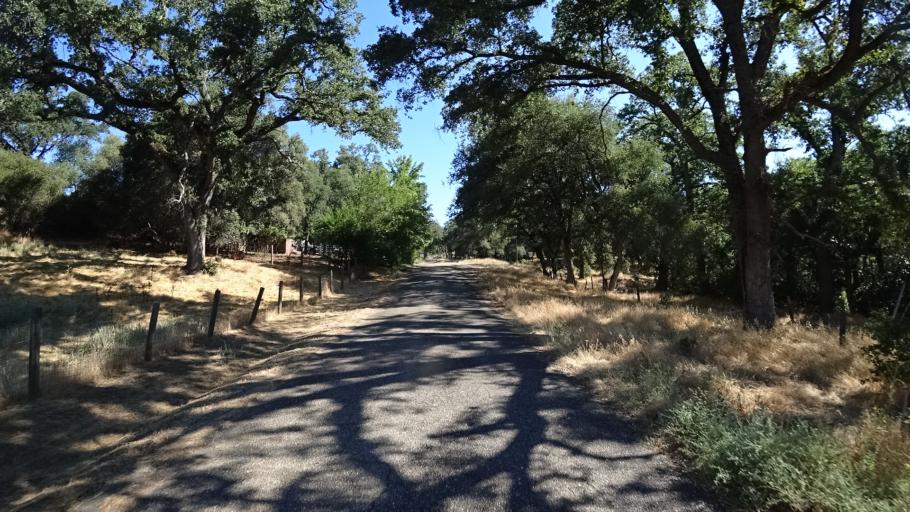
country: US
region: California
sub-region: Calaveras County
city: Murphys
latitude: 38.0992
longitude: -120.4699
